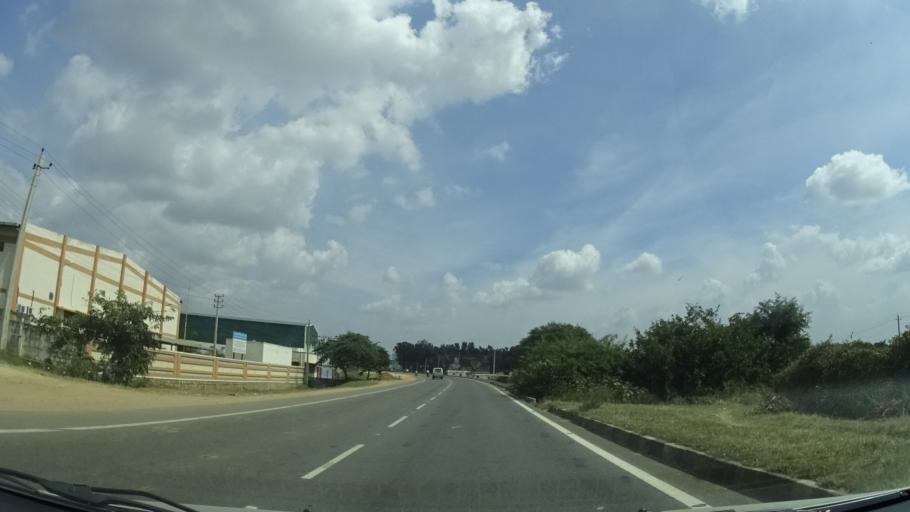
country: IN
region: Karnataka
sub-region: Bangalore Rural
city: Nelamangala
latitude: 13.1526
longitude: 77.3346
